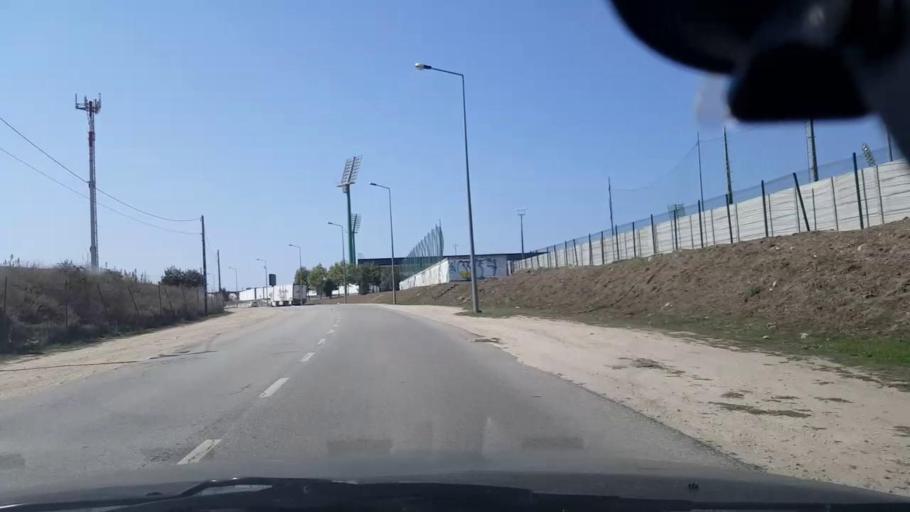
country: PT
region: Porto
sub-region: Vila do Conde
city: Vila do Conde
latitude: 41.3621
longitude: -8.7371
